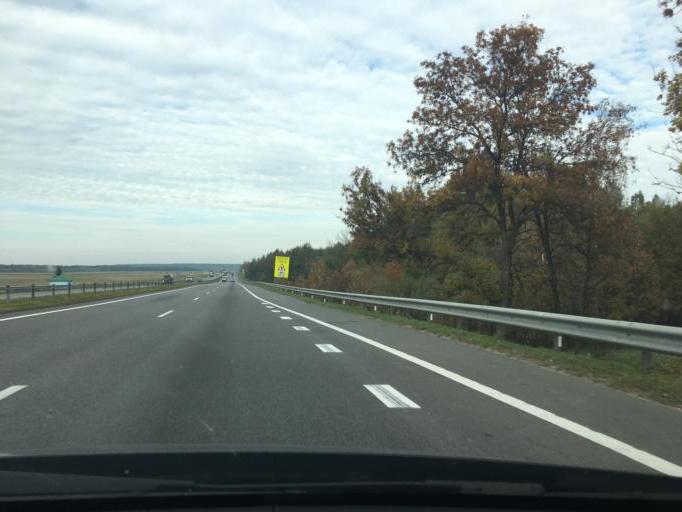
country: BY
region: Minsk
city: Enyerhyetykaw
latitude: 53.5998
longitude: 27.0442
